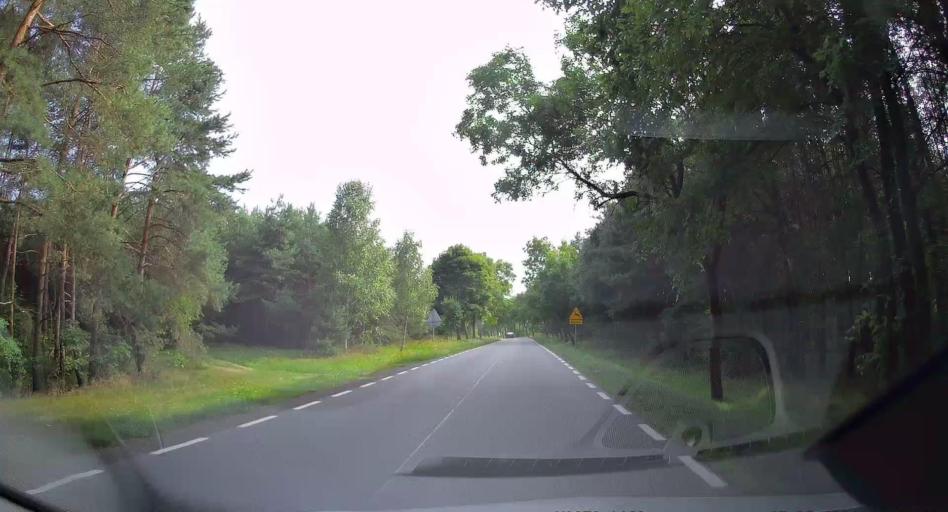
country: PL
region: Lodz Voivodeship
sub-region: Powiat tomaszowski
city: Inowlodz
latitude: 51.5383
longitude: 20.2329
